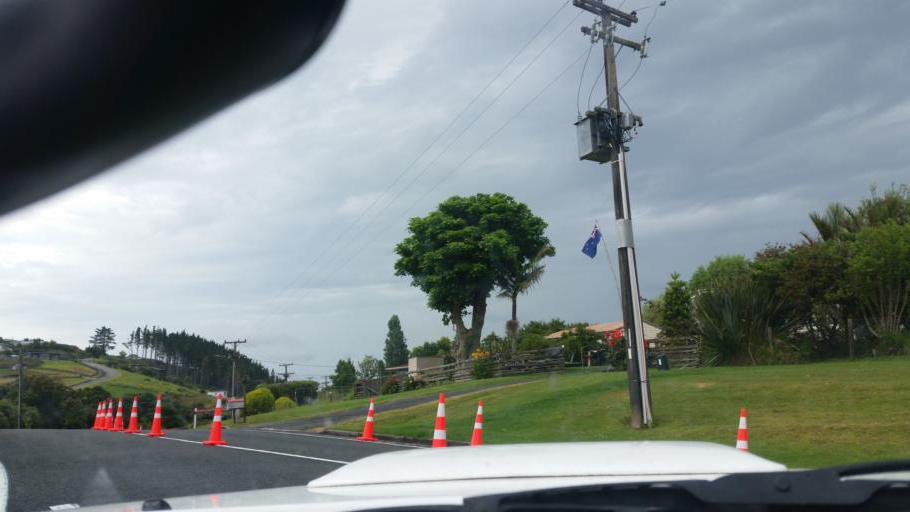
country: NZ
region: Auckland
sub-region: Auckland
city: Wellsford
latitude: -36.1529
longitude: 174.2226
